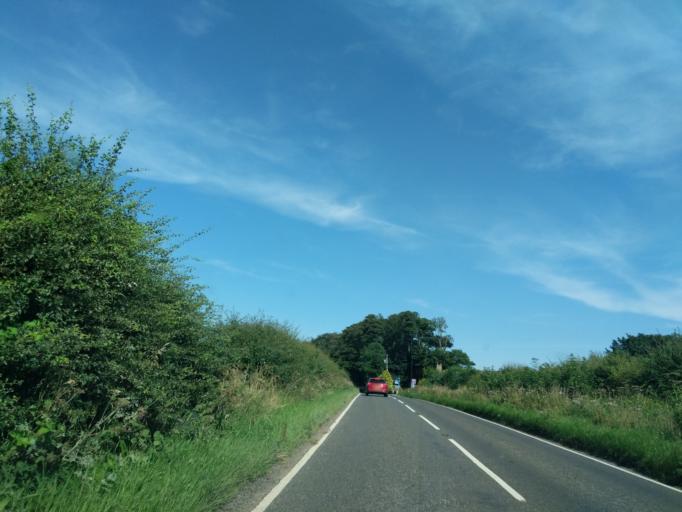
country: GB
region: Scotland
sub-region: Fife
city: Anstruther
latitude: 56.3119
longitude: -2.6879
